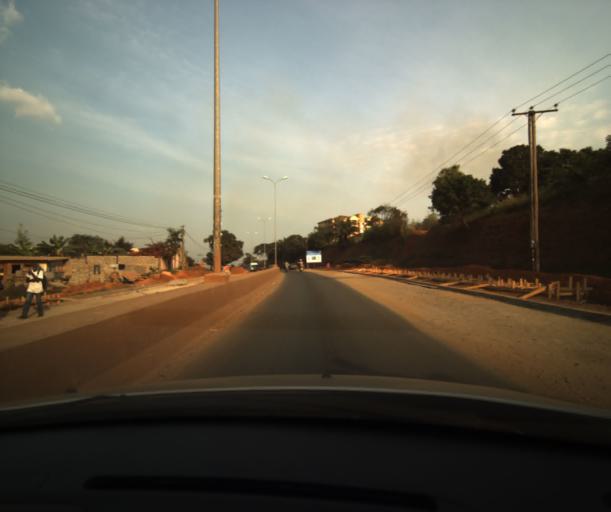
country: CM
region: Centre
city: Yaounde
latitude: 3.8714
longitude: 11.4661
